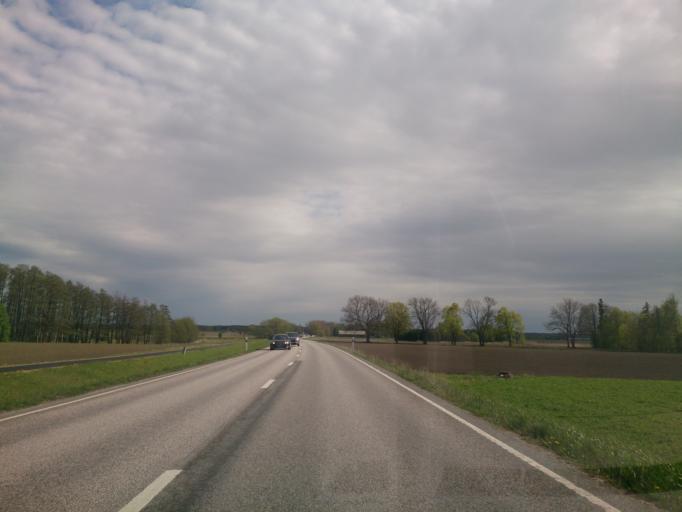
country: SE
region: OEstergoetland
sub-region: Linkopings Kommun
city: Berg
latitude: 58.4754
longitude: 15.5259
